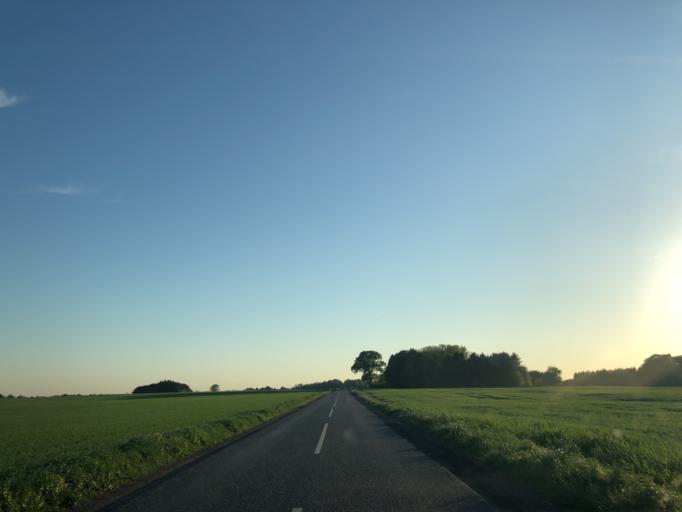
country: DK
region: Zealand
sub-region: Faxe Kommune
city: Haslev
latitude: 55.4119
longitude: 11.9081
